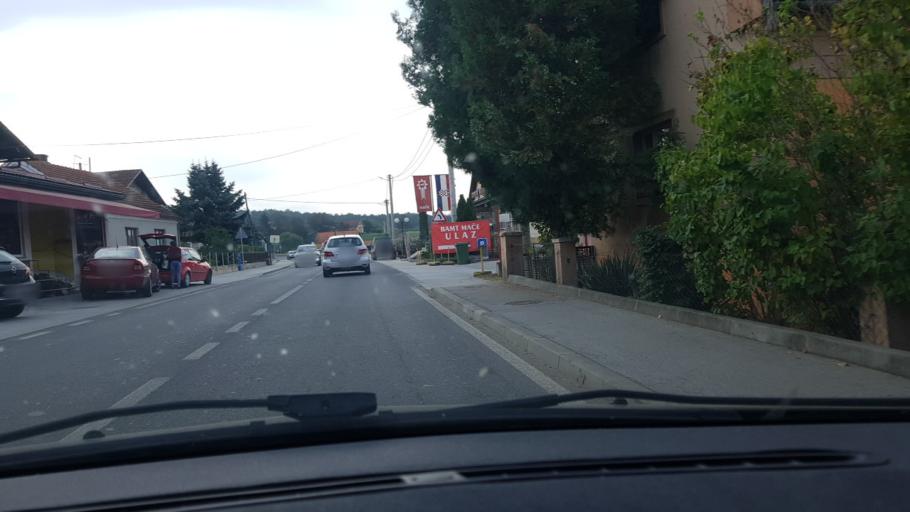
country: HR
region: Krapinsko-Zagorska
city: Zlatar
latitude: 46.0931
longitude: 16.0439
